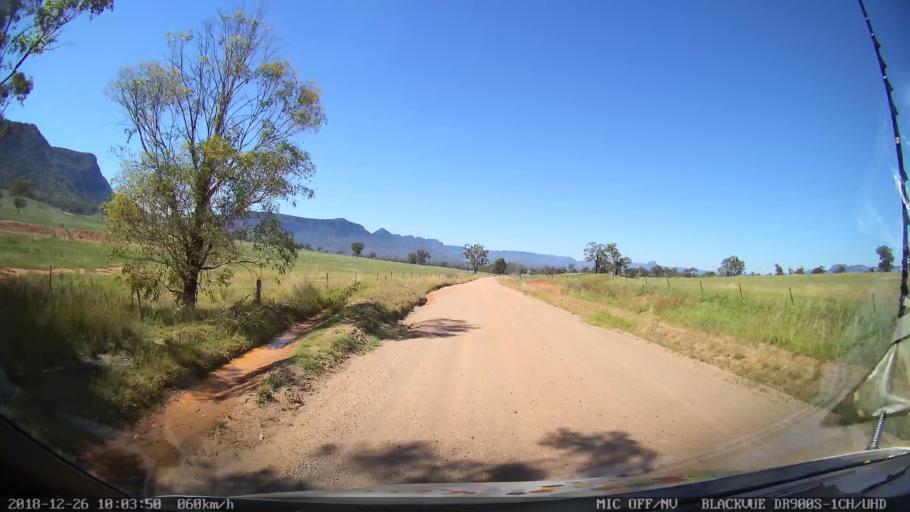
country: AU
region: New South Wales
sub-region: Mid-Western Regional
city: Kandos
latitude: -33.0650
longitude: 150.2167
